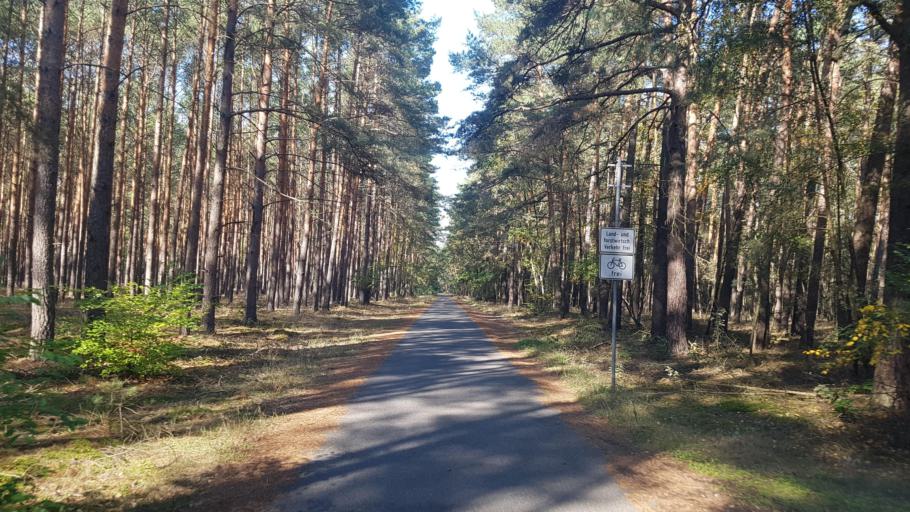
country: DE
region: Brandenburg
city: Ihlow
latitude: 51.8653
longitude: 13.2555
